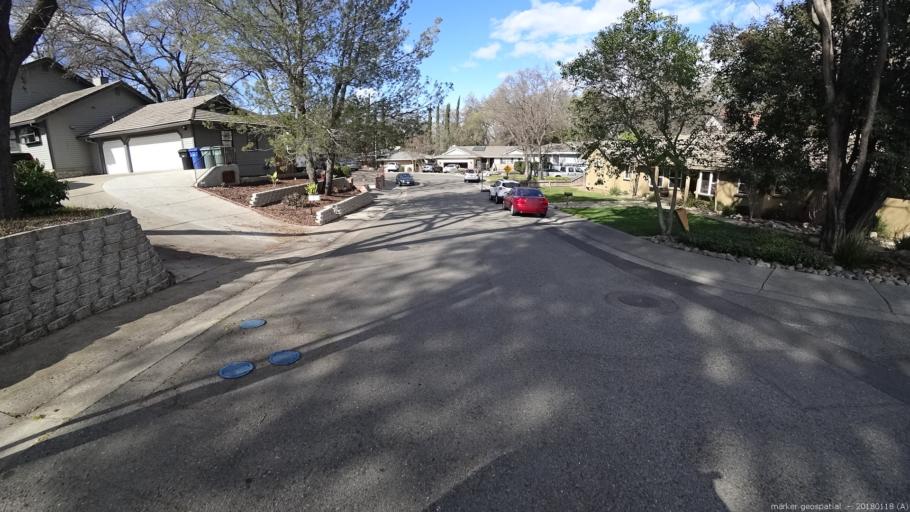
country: US
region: California
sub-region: Sacramento County
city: Orangevale
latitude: 38.6746
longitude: -121.2082
